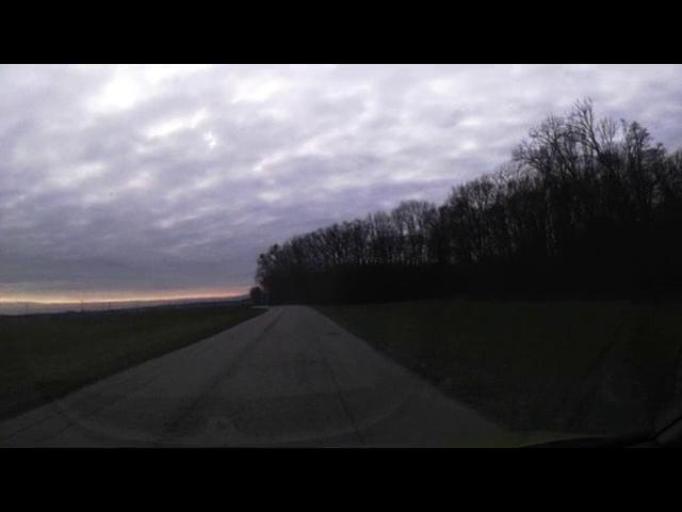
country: AT
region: Lower Austria
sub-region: Politischer Bezirk Wiener Neustadt
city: Ebenfurth
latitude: 47.8947
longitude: 16.3508
